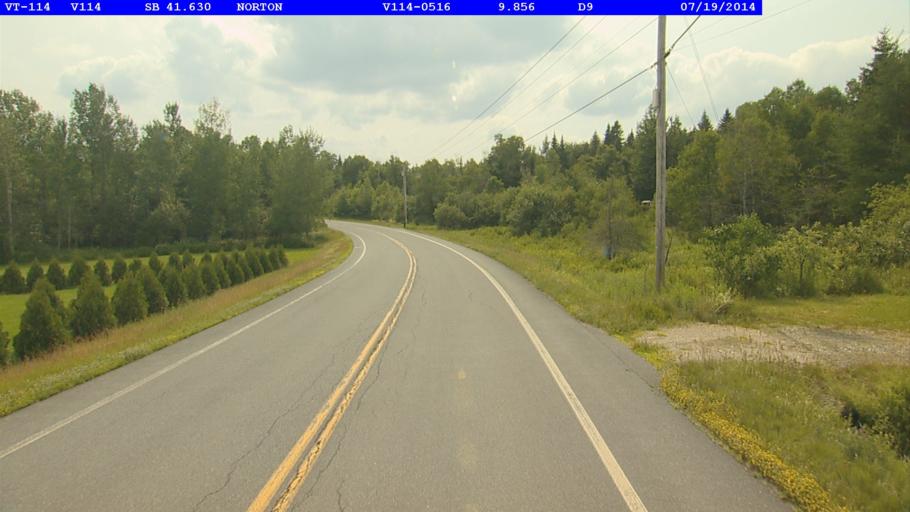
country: CA
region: Quebec
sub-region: Estrie
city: Coaticook
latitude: 44.9985
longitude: -71.7104
